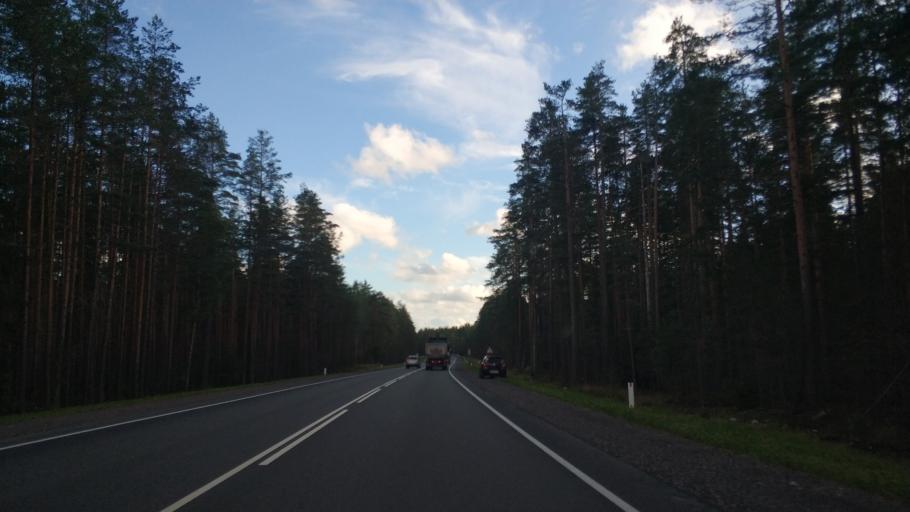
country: RU
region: Leningrad
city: Priozersk
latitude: 60.8845
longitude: 30.1608
